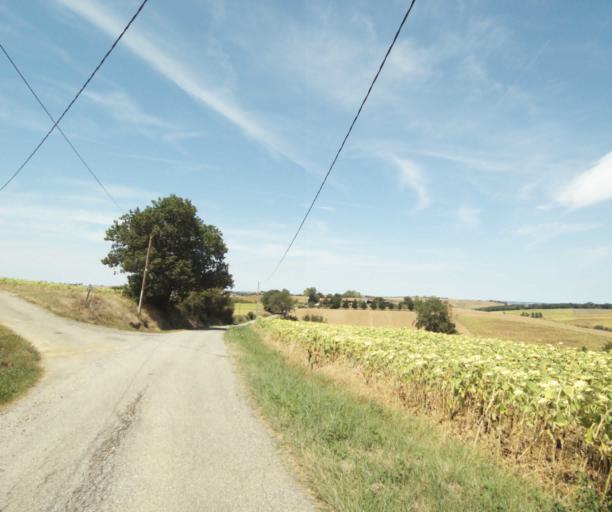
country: FR
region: Midi-Pyrenees
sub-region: Departement de l'Ariege
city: Lezat-sur-Leze
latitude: 43.2827
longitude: 1.3042
